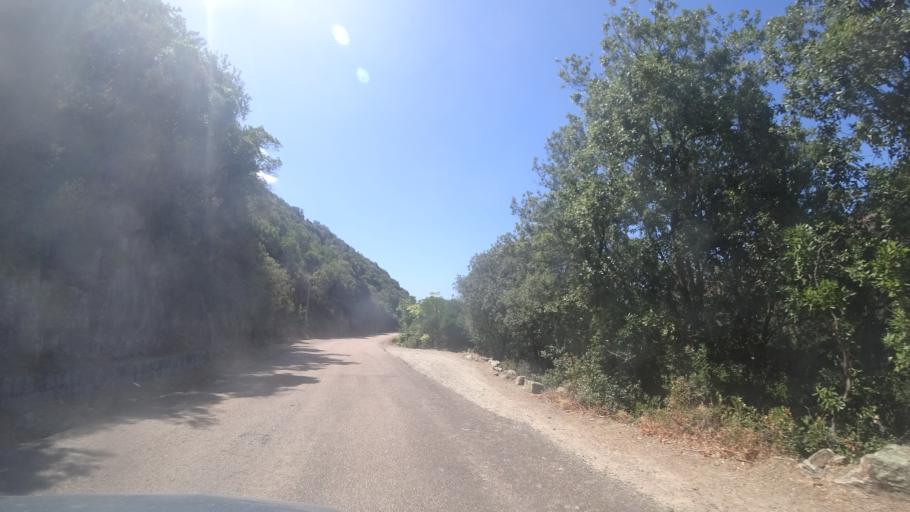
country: FR
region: Corsica
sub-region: Departement de la Corse-du-Sud
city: Cargese
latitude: 42.2630
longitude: 8.6997
